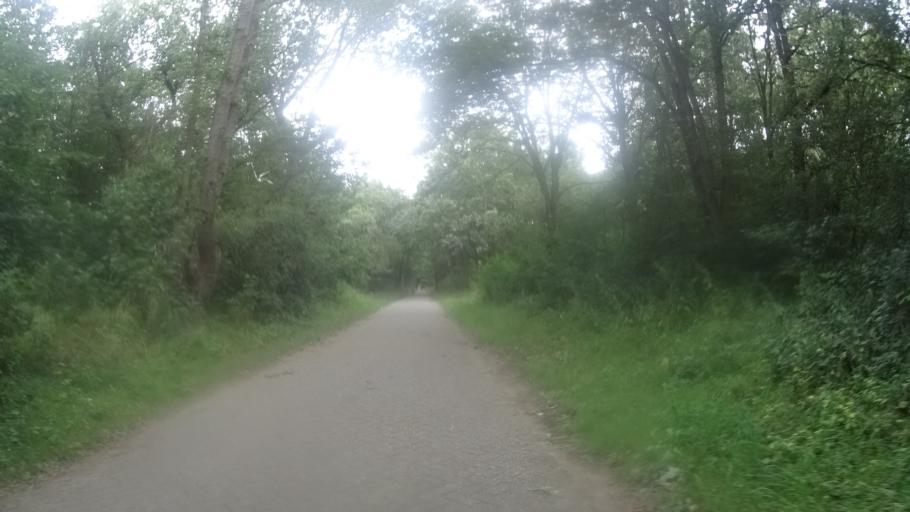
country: NL
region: North Holland
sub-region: Gemeente Castricum
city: Castricum
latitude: 52.5581
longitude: 4.6365
